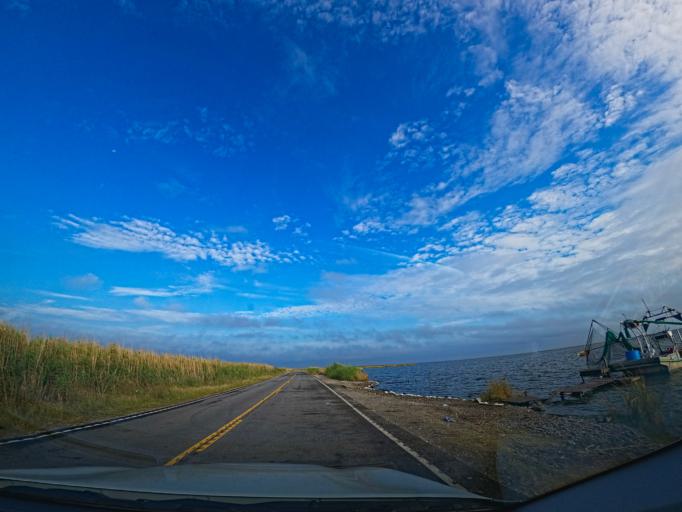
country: US
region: Louisiana
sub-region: Terrebonne Parish
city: Dulac
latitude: 29.3015
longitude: -90.6690
